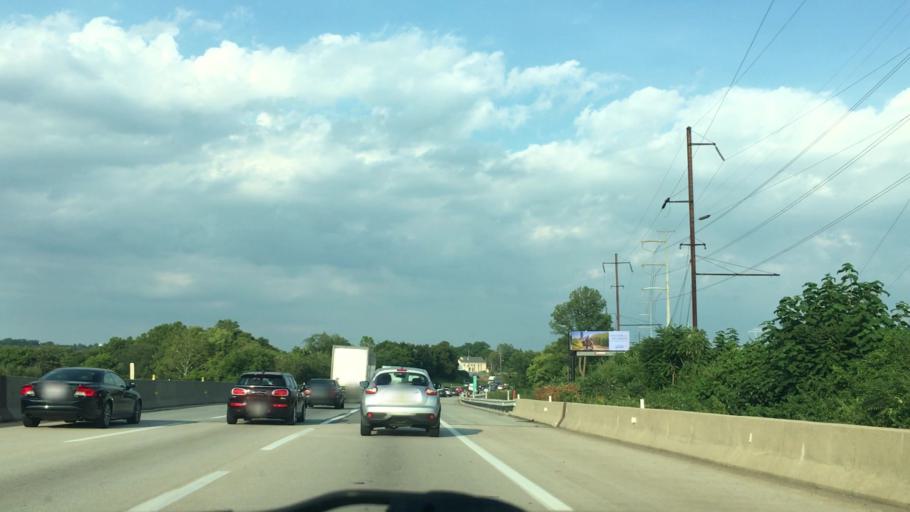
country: US
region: Pennsylvania
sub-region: Montgomery County
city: Bridgeport
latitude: 40.1045
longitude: -75.3210
